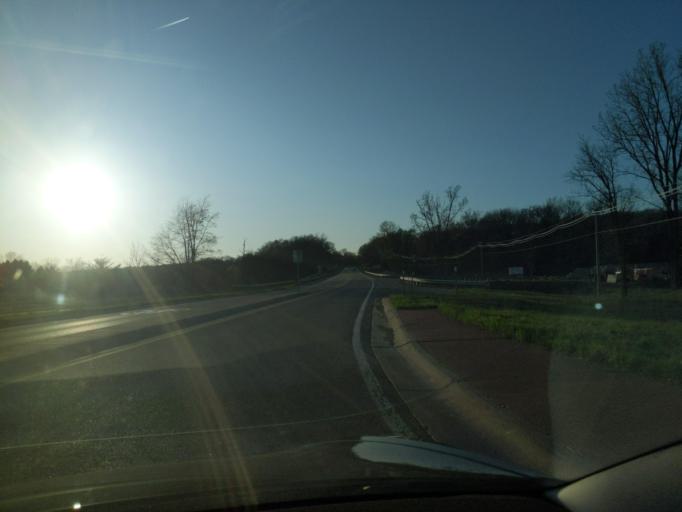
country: US
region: Michigan
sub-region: Washtenaw County
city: Chelsea
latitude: 42.3369
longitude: -84.0290
